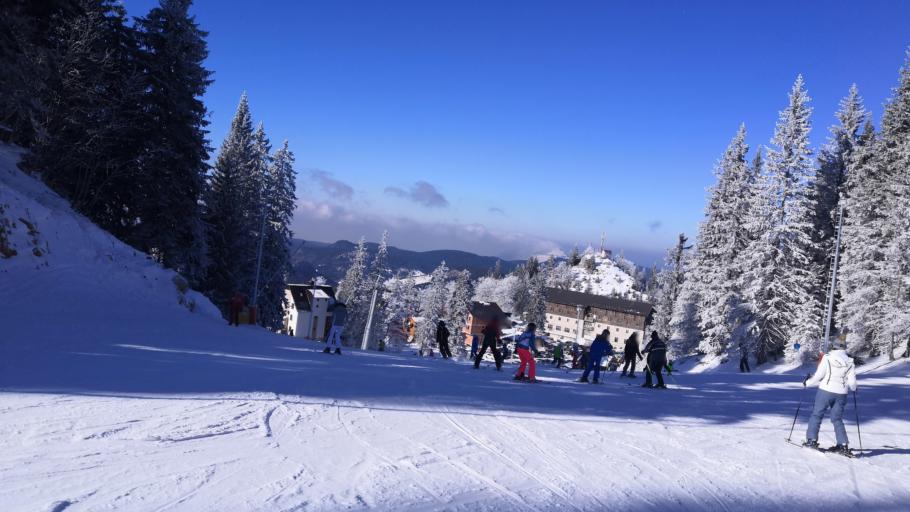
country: BA
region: Republika Srpska
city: Koran
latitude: 43.7300
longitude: 18.5654
